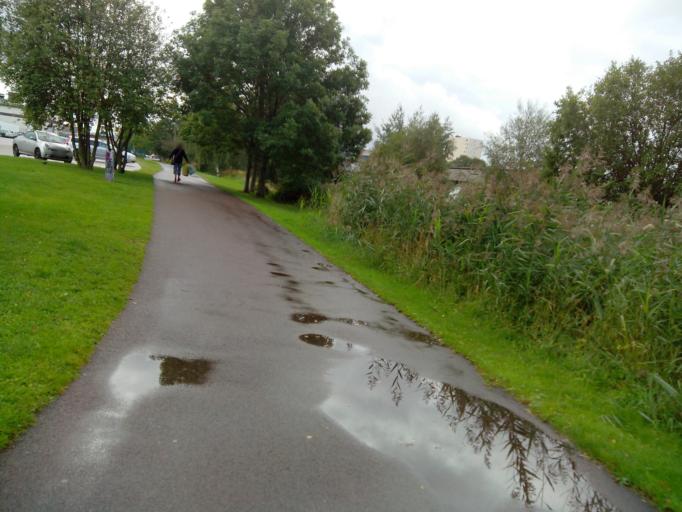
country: SE
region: Vaestra Goetaland
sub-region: Goteborg
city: Goeteborg
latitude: 57.7275
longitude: 11.9514
